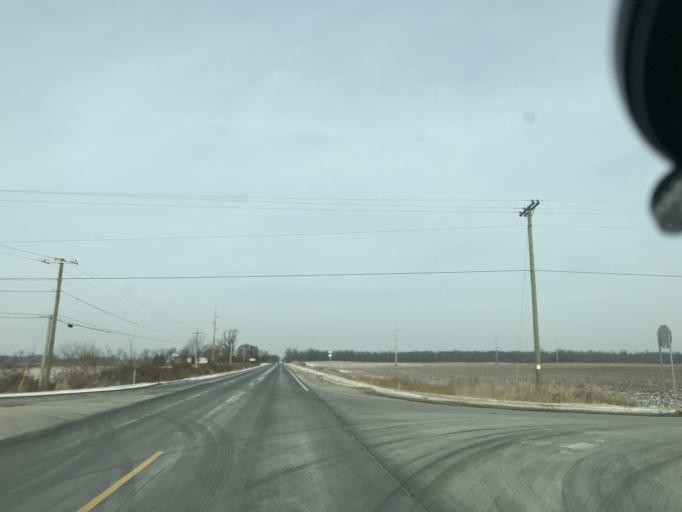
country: US
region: Michigan
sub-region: Ionia County
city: Lake Odessa
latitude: 42.8428
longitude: -85.0749
